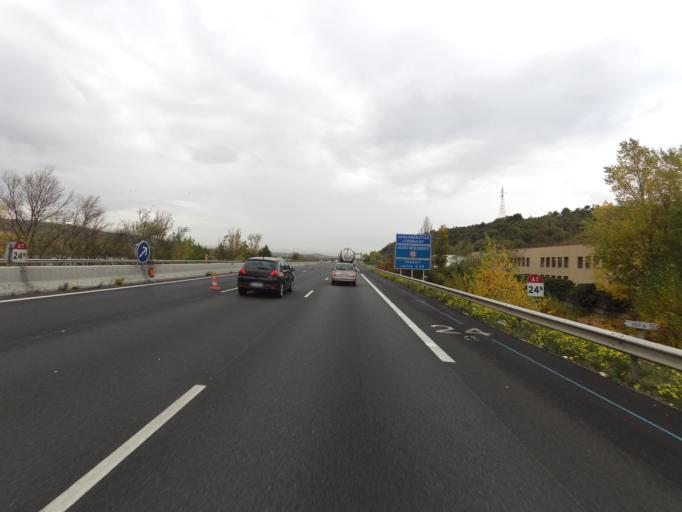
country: FR
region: Rhone-Alpes
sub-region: Departement du Rhone
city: Loire-sur-Rhone
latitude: 45.5582
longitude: 4.8235
